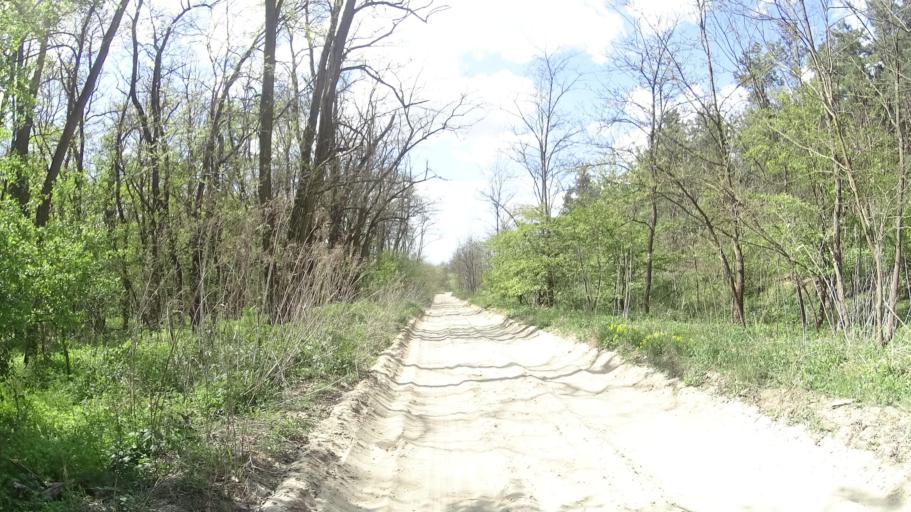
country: HU
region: Pest
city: Szada
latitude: 47.6052
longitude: 19.3052
